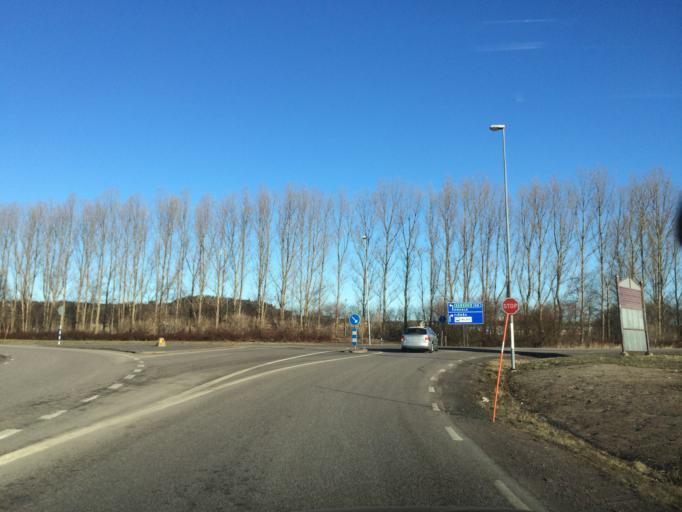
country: SE
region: Halland
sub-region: Kungsbacka Kommun
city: Kungsbacka
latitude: 57.4751
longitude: 12.0755
